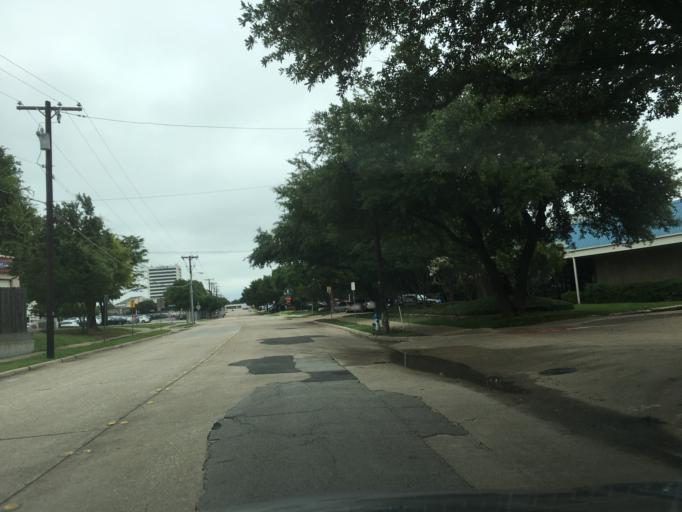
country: US
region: Texas
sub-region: Dallas County
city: Richardson
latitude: 32.9457
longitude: -96.7359
